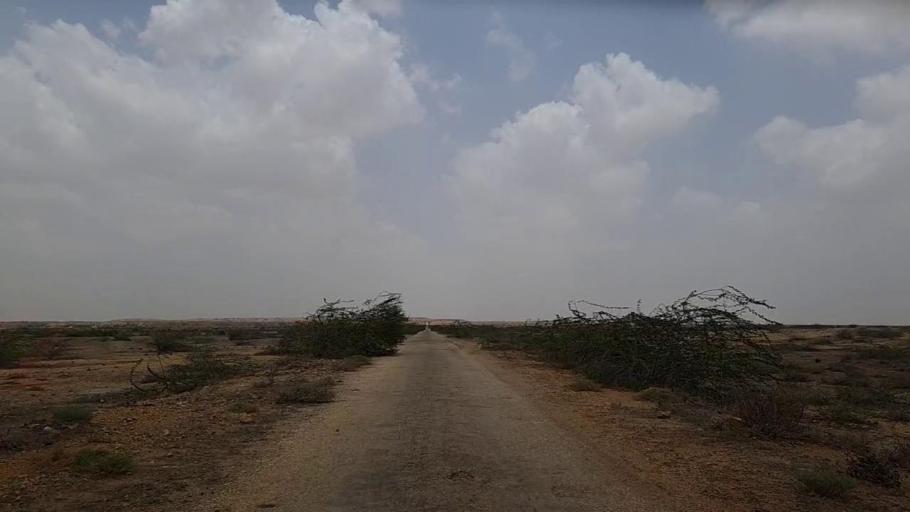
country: PK
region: Sindh
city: Thatta
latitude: 24.8715
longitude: 67.8963
